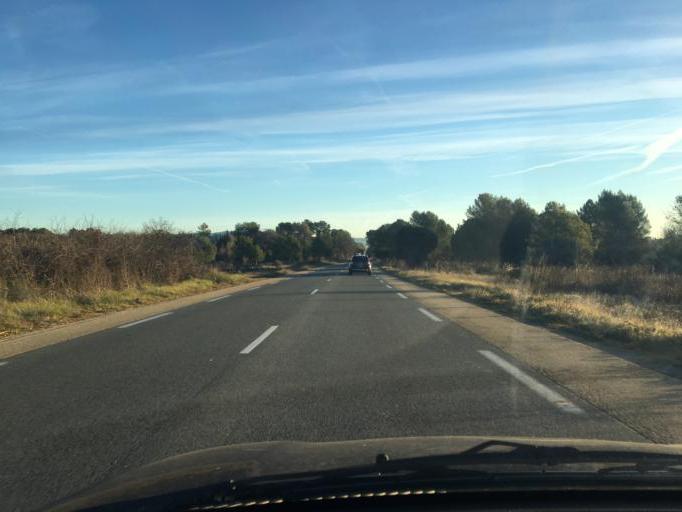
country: FR
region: Provence-Alpes-Cote d'Azur
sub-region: Departement du Var
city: La Motte
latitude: 43.4581
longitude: 6.5197
